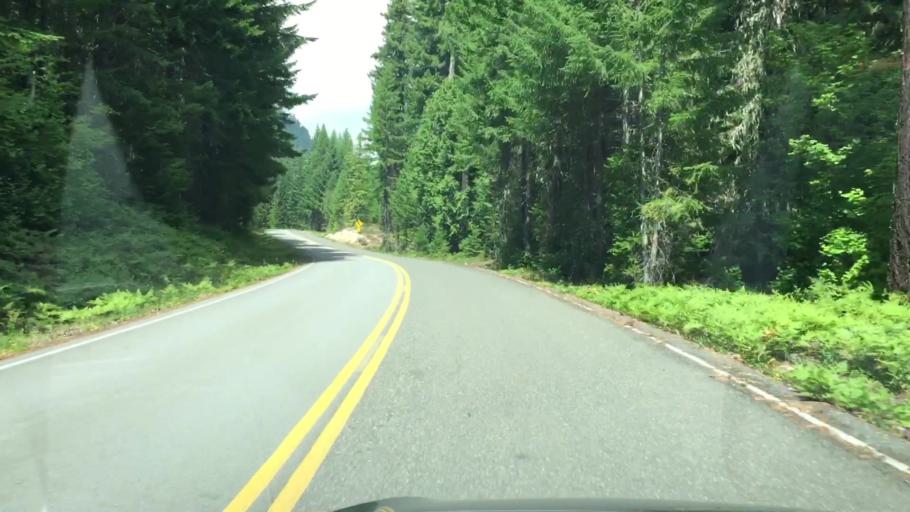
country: US
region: Washington
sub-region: Klickitat County
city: White Salmon
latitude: 46.1043
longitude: -121.6110
